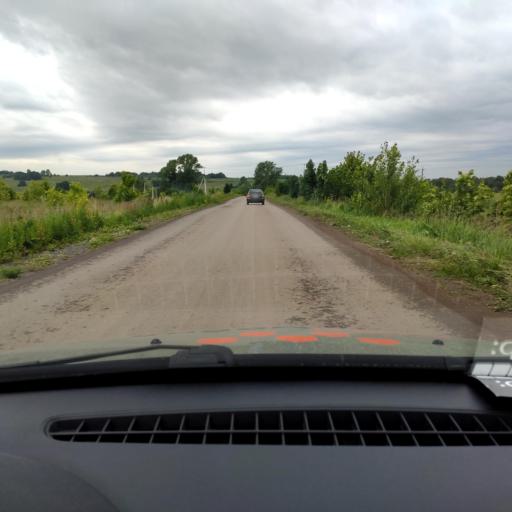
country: RU
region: Bashkortostan
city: Iglino
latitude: 54.8941
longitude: 56.2792
